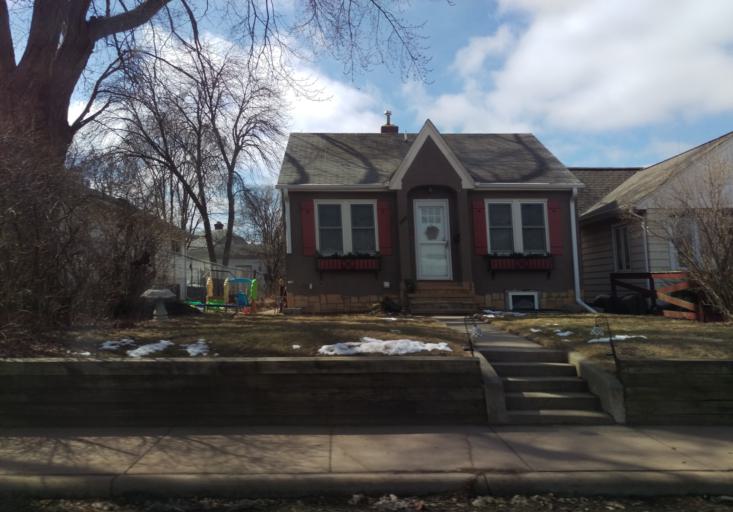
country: US
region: Minnesota
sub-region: Dakota County
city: Mendota Heights
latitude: 44.9081
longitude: -93.2054
